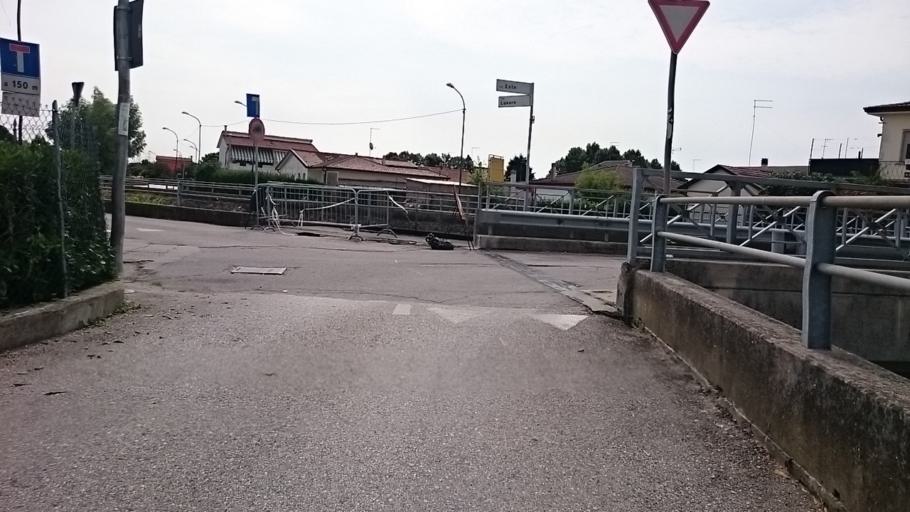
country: IT
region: Veneto
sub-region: Provincia di Venezia
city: Fornase
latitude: 45.4581
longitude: 12.1808
